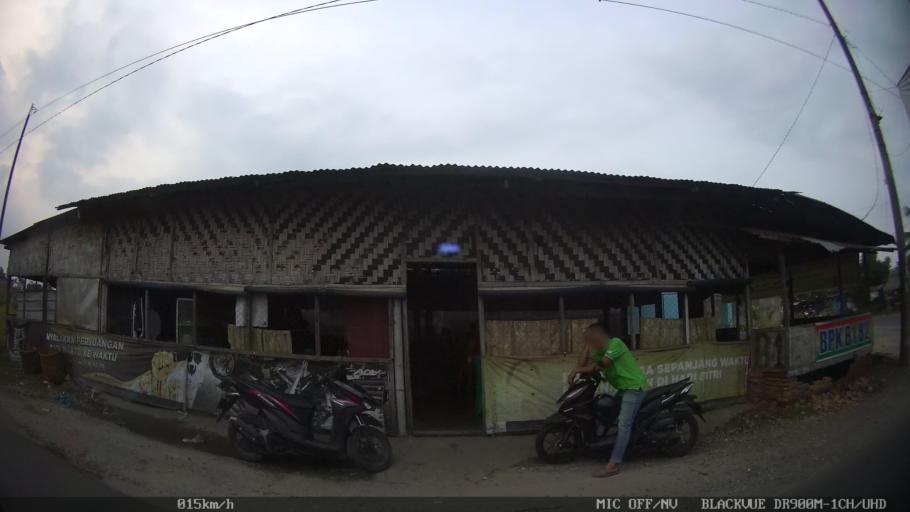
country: ID
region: North Sumatra
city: Sunggal
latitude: 3.5614
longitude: 98.5961
